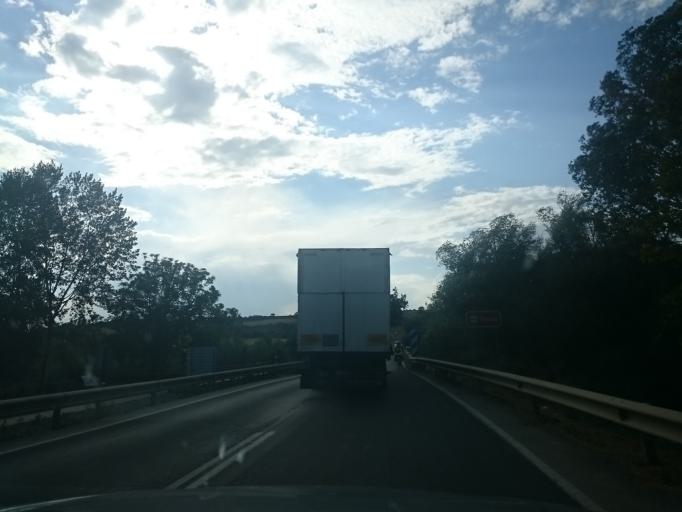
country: ES
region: Castille and Leon
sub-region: Provincia de Burgos
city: Belorado
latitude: 42.4179
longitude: -3.2015
